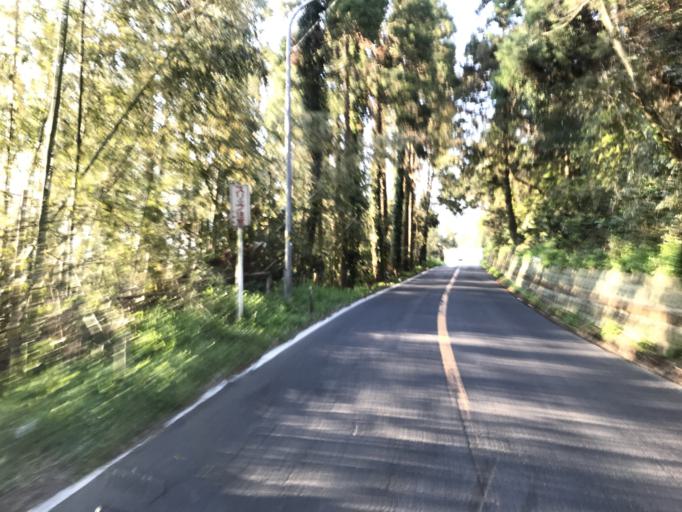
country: JP
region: Chiba
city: Yokaichiba
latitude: 35.7244
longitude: 140.5628
